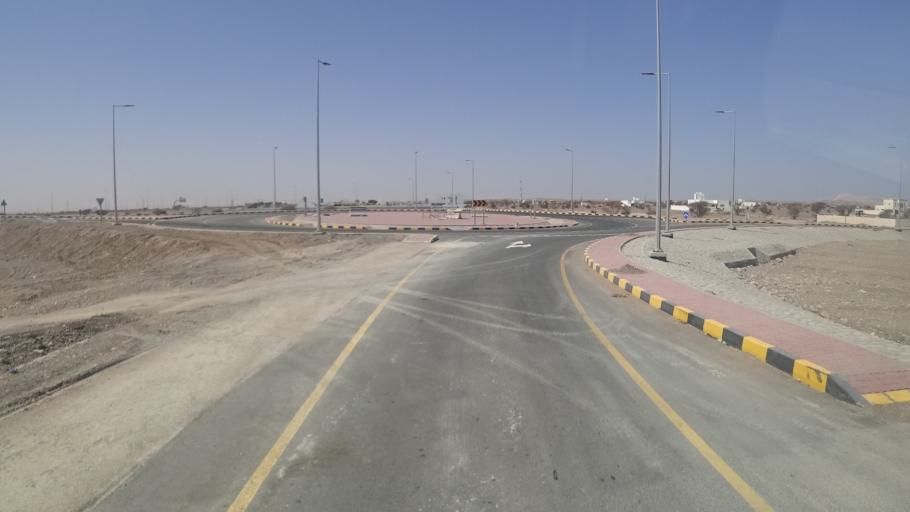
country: OM
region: Ash Sharqiyah
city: Badiyah
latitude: 22.4974
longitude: 58.9472
